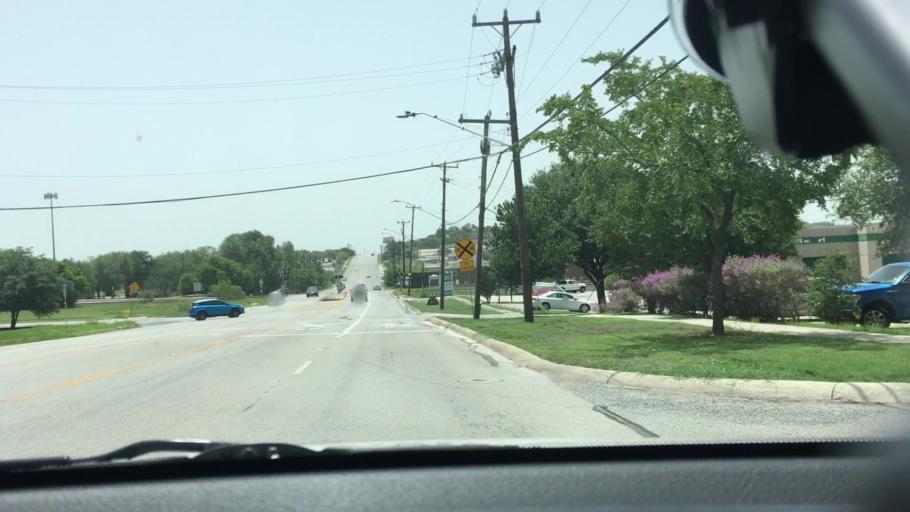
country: US
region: Texas
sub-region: Bexar County
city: Live Oak
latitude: 29.5713
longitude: -98.3575
